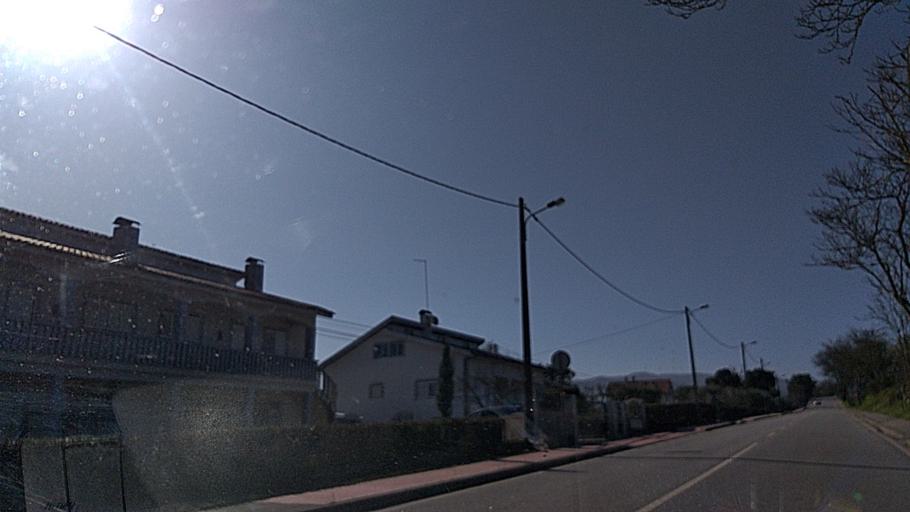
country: PT
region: Guarda
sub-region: Celorico da Beira
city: Celorico da Beira
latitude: 40.6495
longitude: -7.3824
